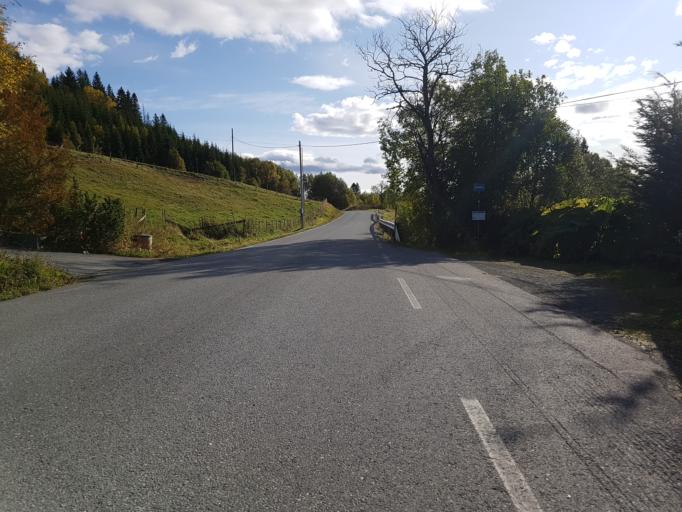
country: NO
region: Sor-Trondelag
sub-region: Malvik
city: Malvik
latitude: 63.3857
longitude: 10.5853
